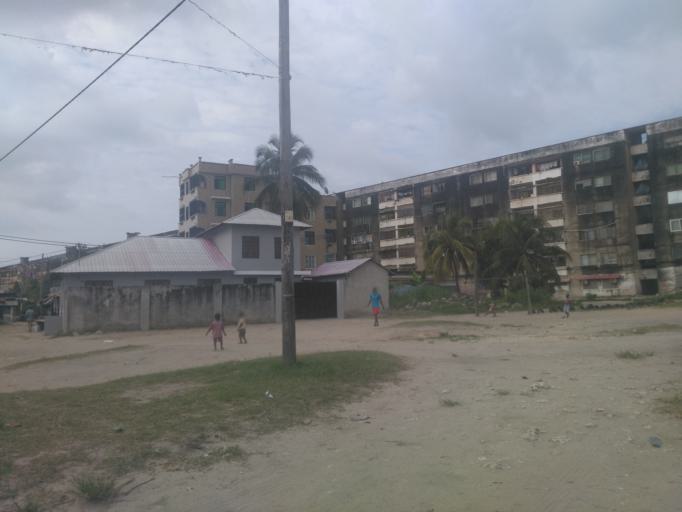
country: TZ
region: Zanzibar Urban/West
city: Zanzibar
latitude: -6.1670
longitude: 39.1997
